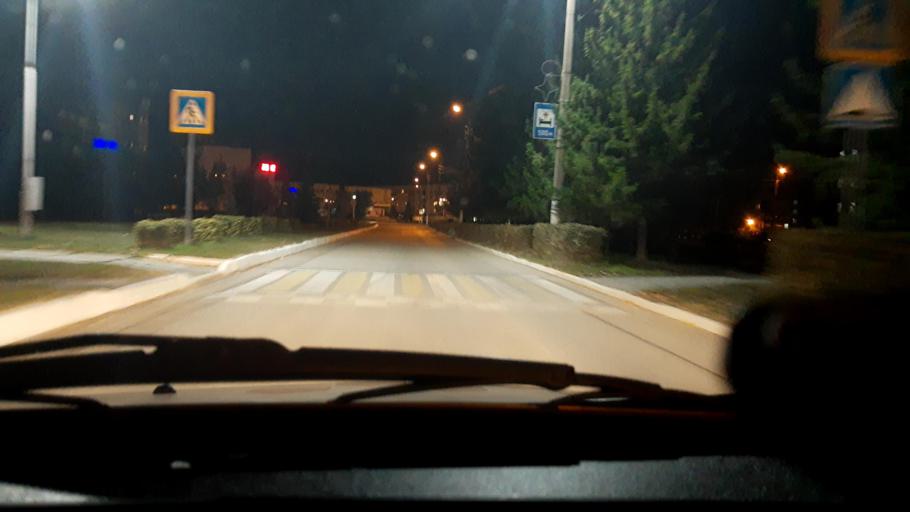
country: RU
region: Bashkortostan
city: Belebey
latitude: 54.1013
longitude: 54.1033
